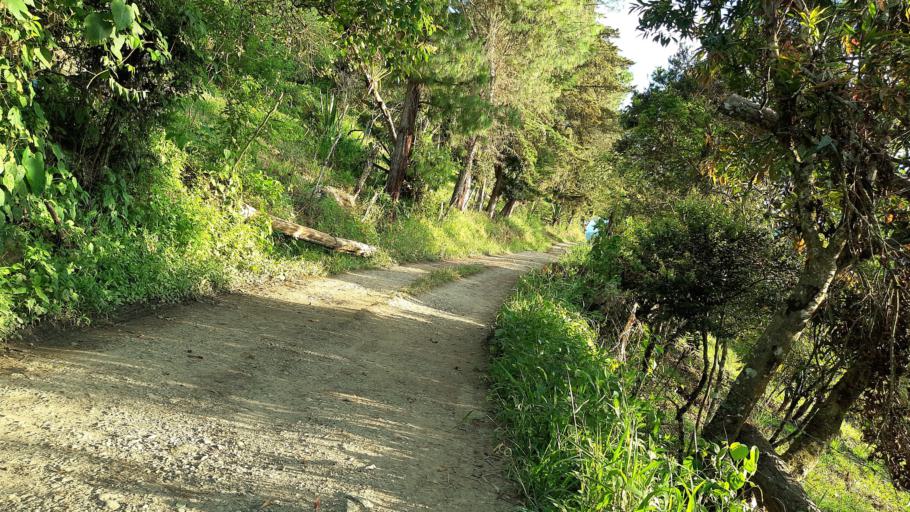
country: CO
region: Boyaca
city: Garagoa
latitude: 5.0651
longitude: -73.3763
